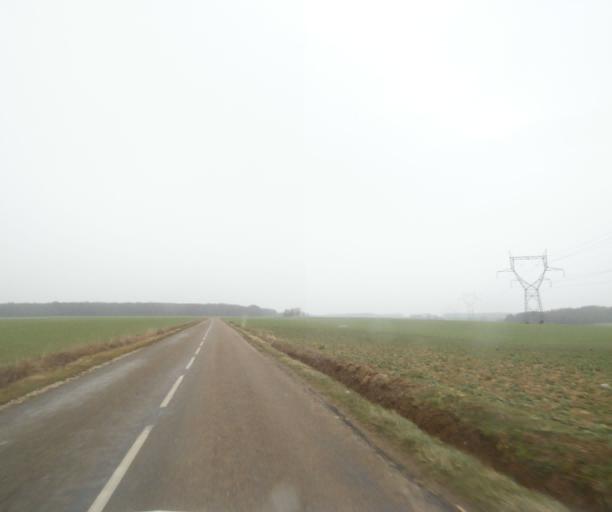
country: FR
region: Champagne-Ardenne
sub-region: Departement de la Haute-Marne
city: Bienville
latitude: 48.5182
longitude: 5.0235
